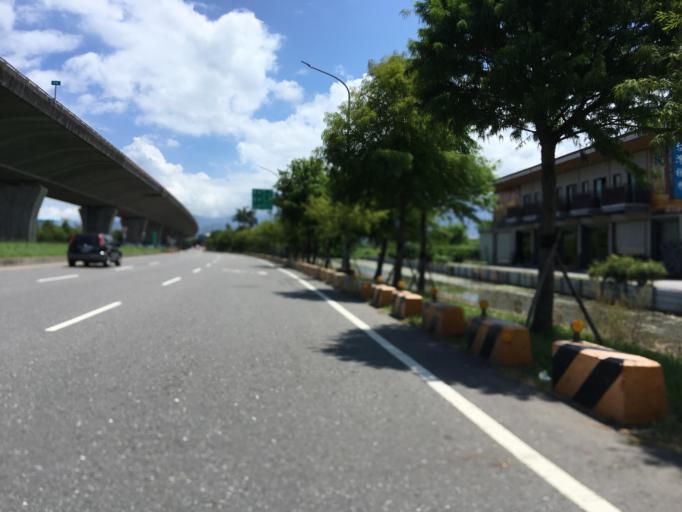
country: TW
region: Taiwan
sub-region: Yilan
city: Yilan
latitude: 24.6923
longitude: 121.7906
